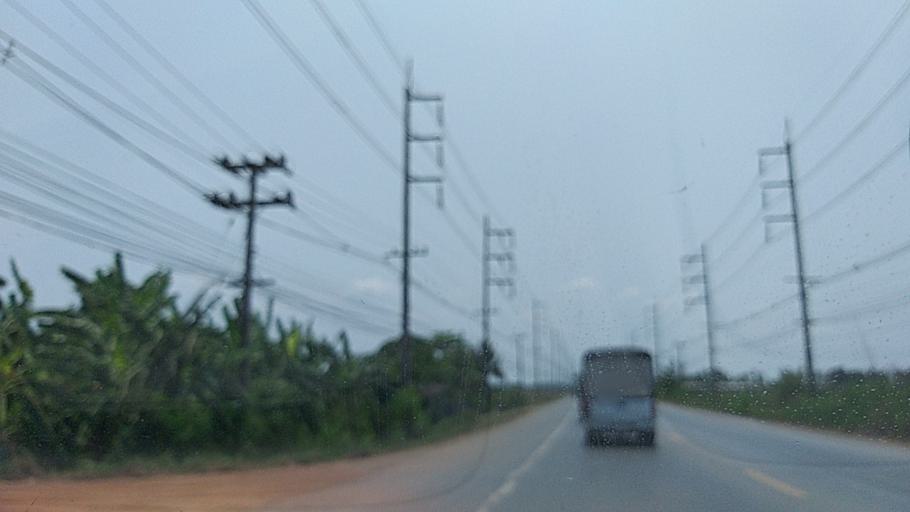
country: TH
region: Chachoengsao
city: Bang Nam Priao
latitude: 13.8219
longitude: 101.0536
